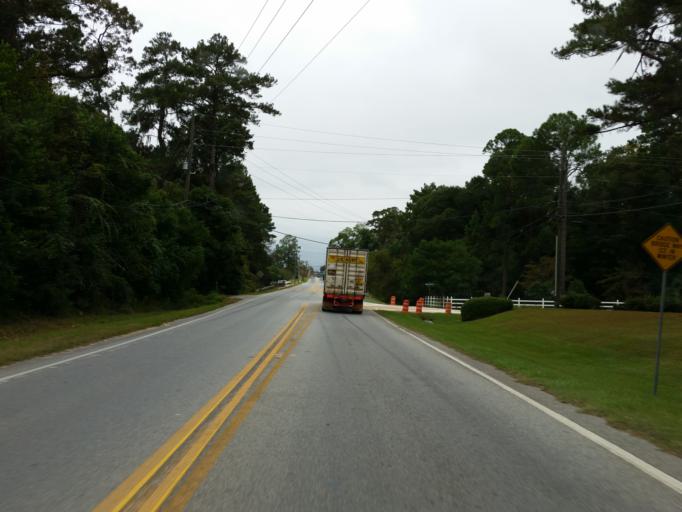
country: US
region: Georgia
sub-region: Cook County
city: Adel
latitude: 31.1393
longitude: -83.4147
